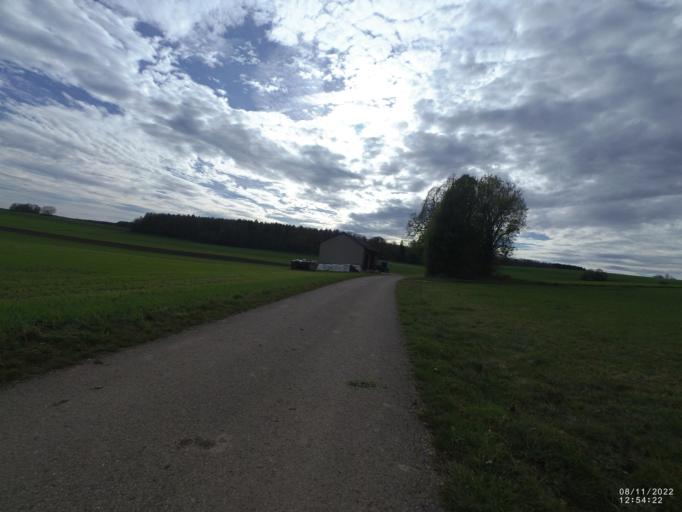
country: DE
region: Baden-Wuerttemberg
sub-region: Tuebingen Region
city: Nellingen
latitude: 48.5731
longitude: 9.7625
